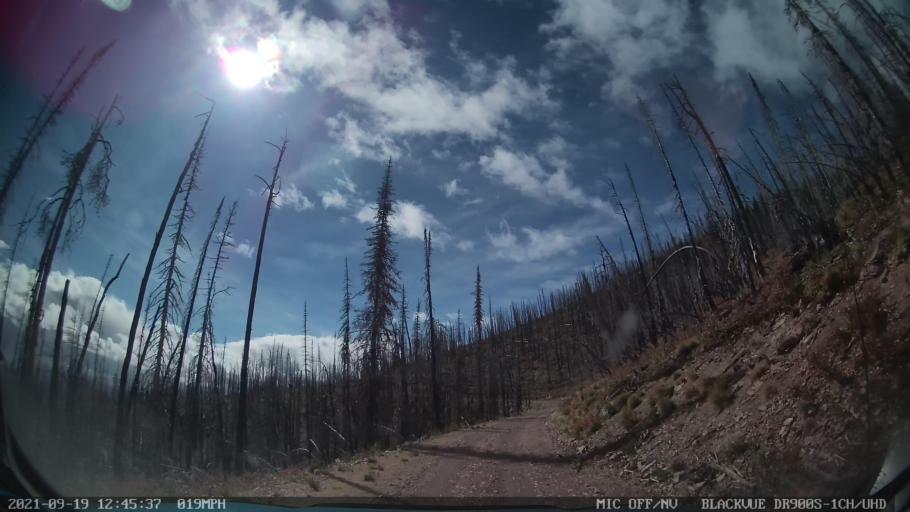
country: US
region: Montana
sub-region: Missoula County
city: Seeley Lake
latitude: 47.1872
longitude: -113.3517
